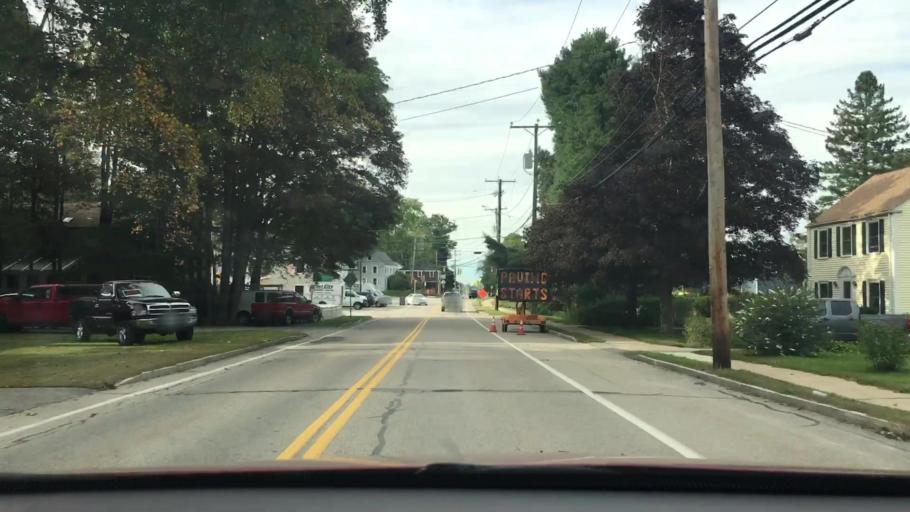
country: US
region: Maine
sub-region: York County
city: South Eliot
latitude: 43.0841
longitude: -70.7864
